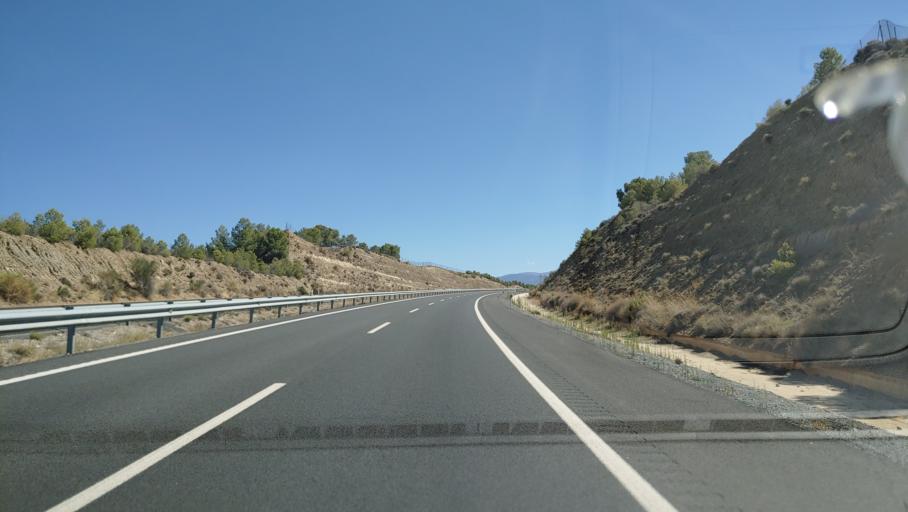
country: ES
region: Andalusia
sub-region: Provincia de Granada
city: Guadix
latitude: 37.2790
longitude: -3.0967
